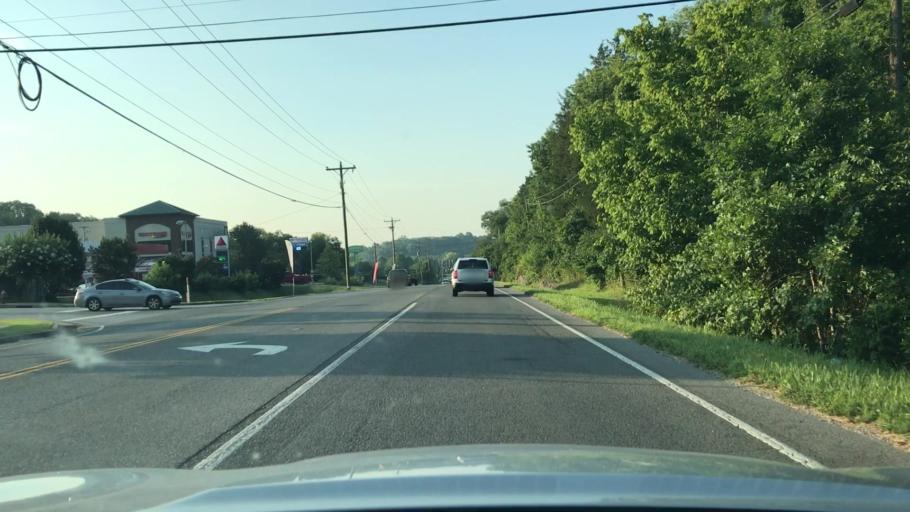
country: US
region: Tennessee
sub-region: Williamson County
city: Nolensville
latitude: 36.0156
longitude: -86.7059
